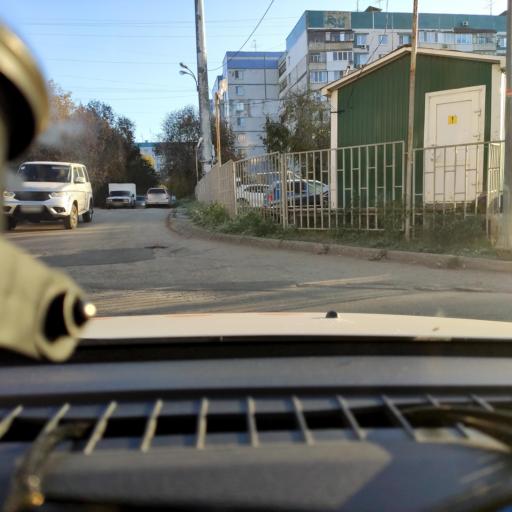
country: RU
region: Samara
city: Samara
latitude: 53.1894
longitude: 50.1436
